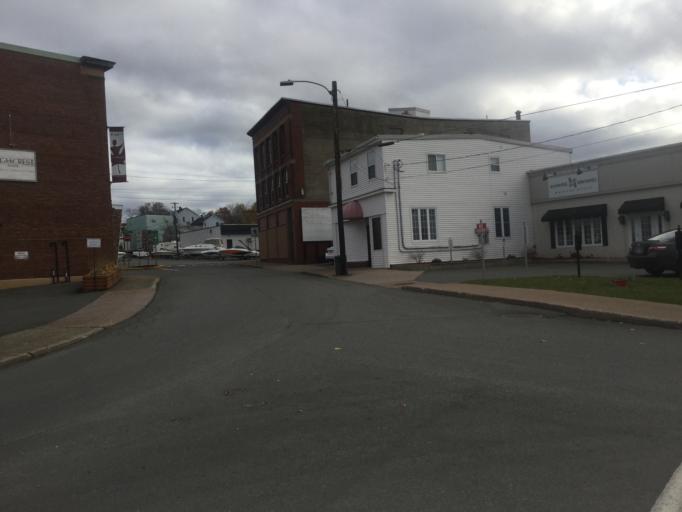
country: CA
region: Nova Scotia
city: New Glasgow
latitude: 45.5858
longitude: -62.6457
